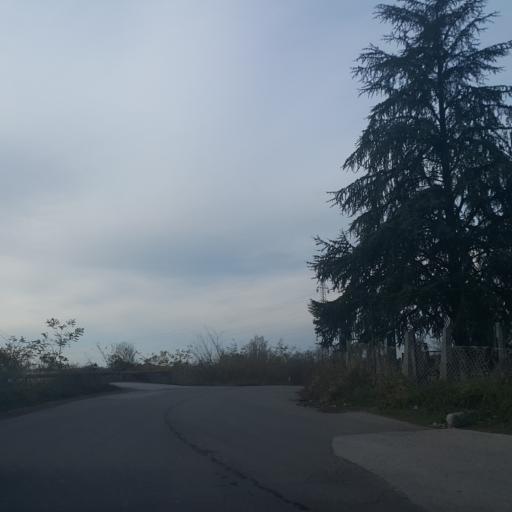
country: RS
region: Central Serbia
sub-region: Belgrade
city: Lazarevac
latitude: 44.4209
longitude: 20.2982
